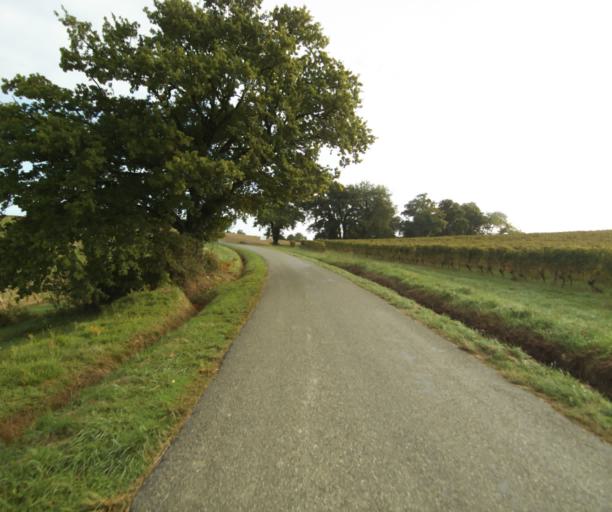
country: FR
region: Midi-Pyrenees
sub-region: Departement du Gers
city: Nogaro
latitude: 43.8294
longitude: -0.0334
